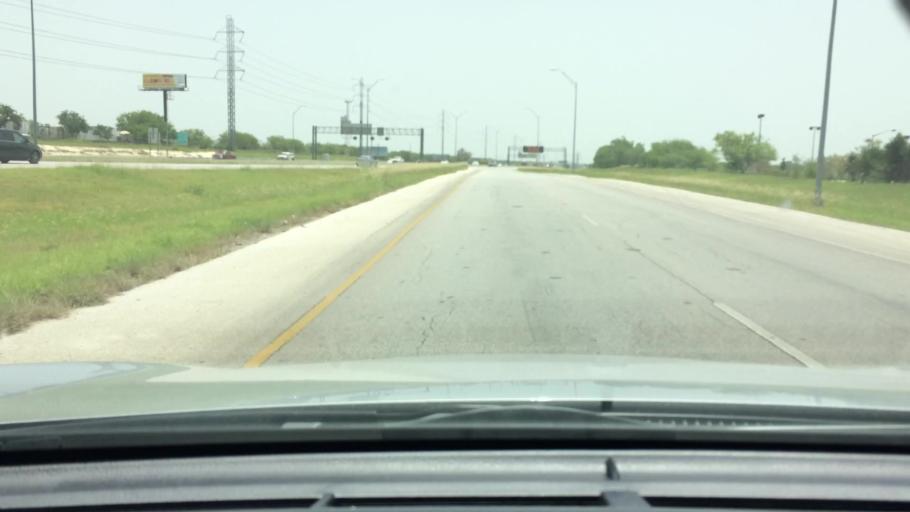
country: US
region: Texas
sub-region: Bexar County
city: China Grove
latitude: 29.3498
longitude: -98.4269
